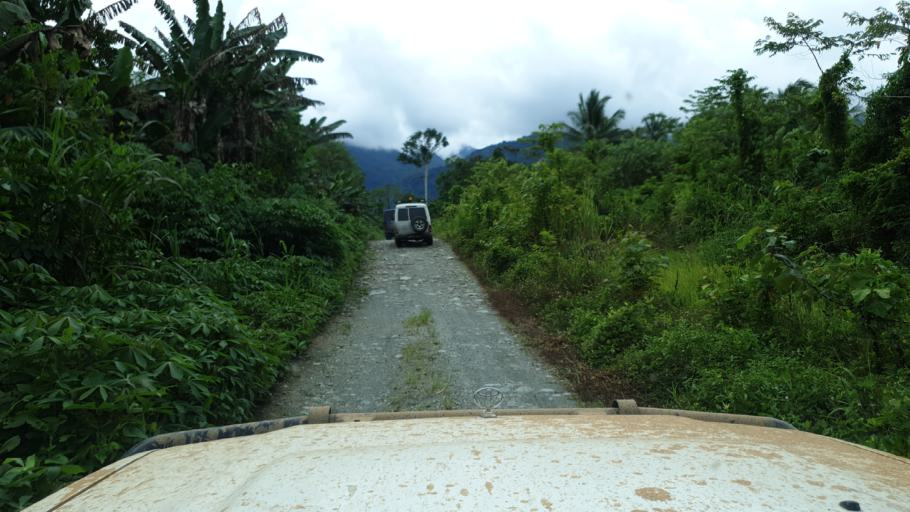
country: PG
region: Northern Province
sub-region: Sohe
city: Kokoda
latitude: -8.9335
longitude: 147.8678
